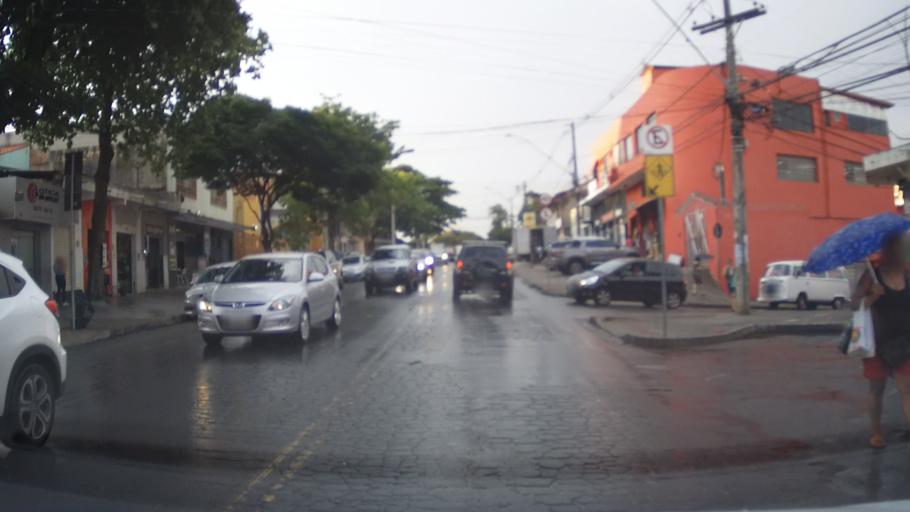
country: BR
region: Minas Gerais
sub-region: Belo Horizonte
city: Belo Horizonte
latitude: -19.9672
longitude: -43.9814
